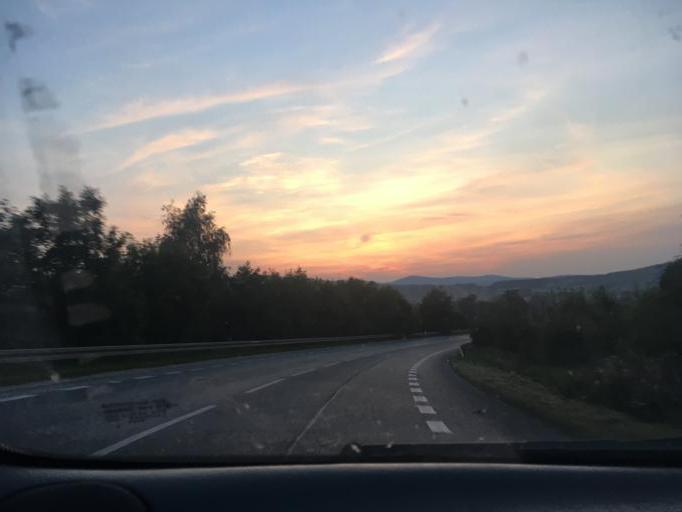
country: PL
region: Lower Silesian Voivodeship
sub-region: Powiat walbrzyski
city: Czarny Bor
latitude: 50.7706
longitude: 16.1366
